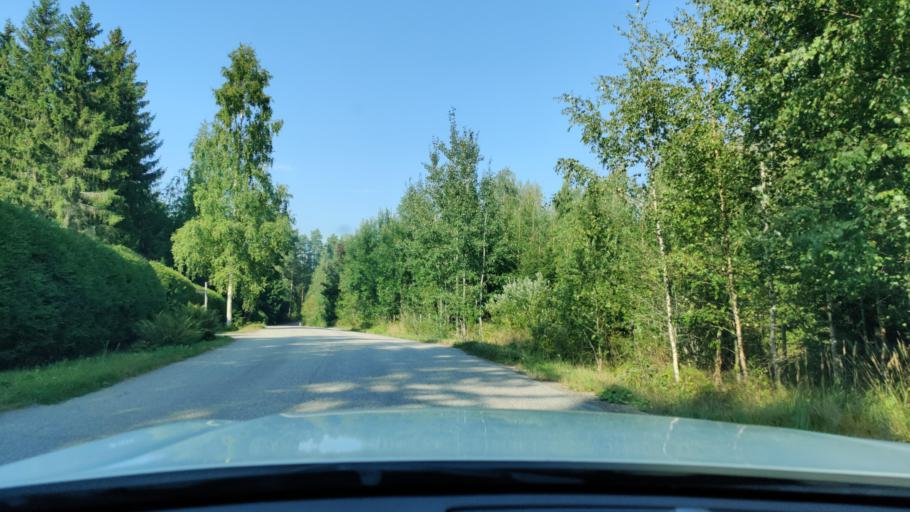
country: FI
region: Haeme
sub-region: Haemeenlinna
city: Tervakoski
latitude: 60.6759
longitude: 24.6292
